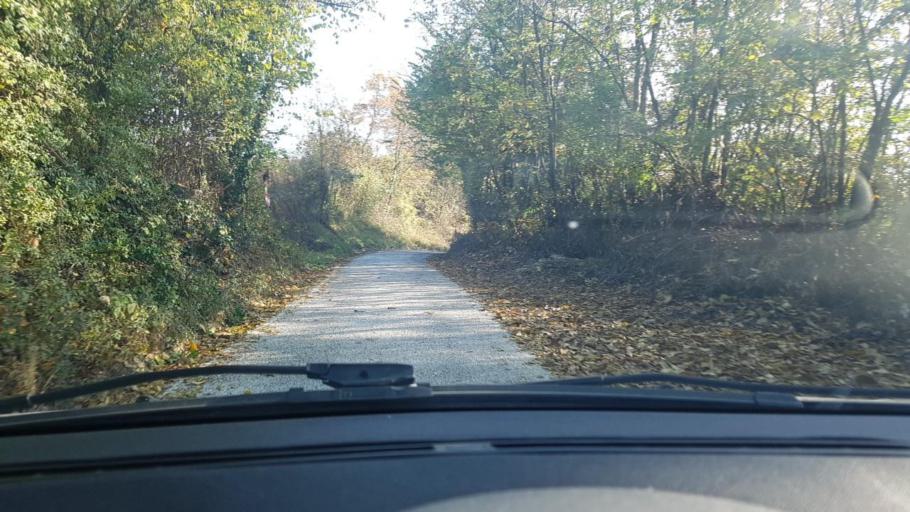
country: HR
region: Krapinsko-Zagorska
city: Zabok
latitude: 46.0388
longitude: 15.8837
